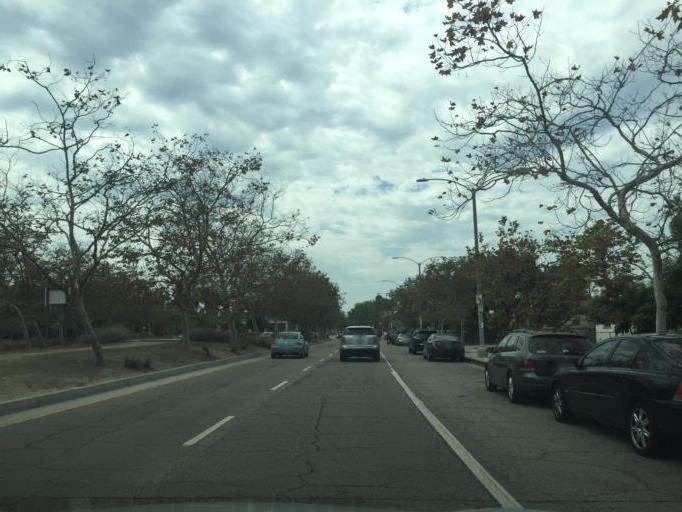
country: US
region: California
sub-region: Los Angeles County
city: Marina del Rey
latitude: 33.9889
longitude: -118.4631
